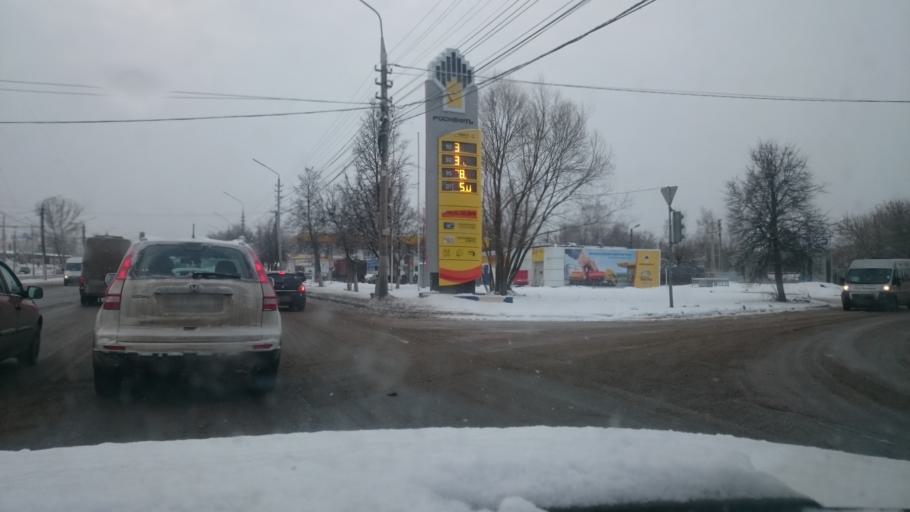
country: RU
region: Tula
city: Mendeleyevskiy
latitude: 54.1475
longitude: 37.5825
